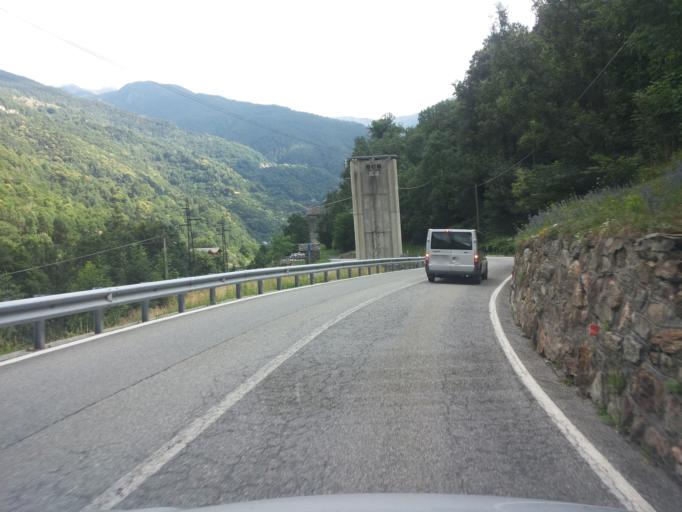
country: IT
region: Aosta Valley
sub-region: Valle d'Aosta
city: Fontainemore
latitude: 45.6625
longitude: 7.8580
